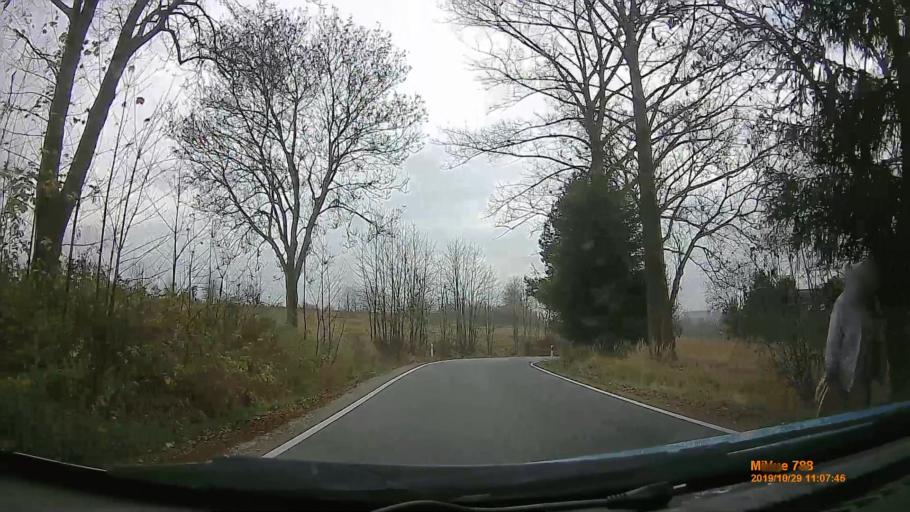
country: PL
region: Lower Silesian Voivodeship
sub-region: Powiat klodzki
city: Polanica-Zdroj
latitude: 50.4550
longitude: 16.4906
